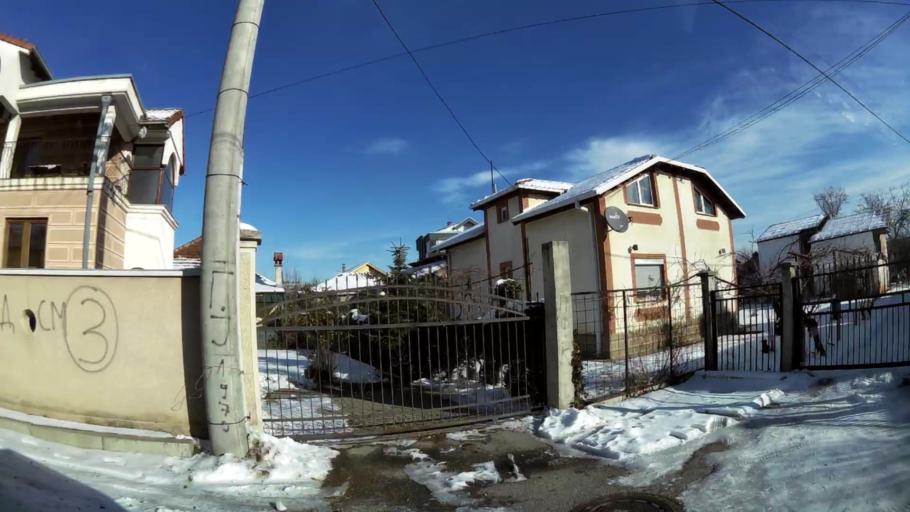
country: MK
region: Saraj
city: Saraj
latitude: 42.0063
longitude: 21.3399
